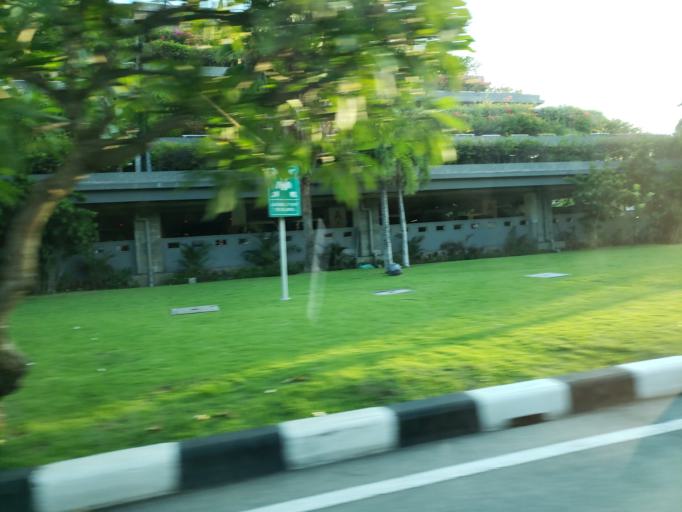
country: ID
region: Bali
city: Kelanabian
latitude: -8.7409
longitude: 115.1661
